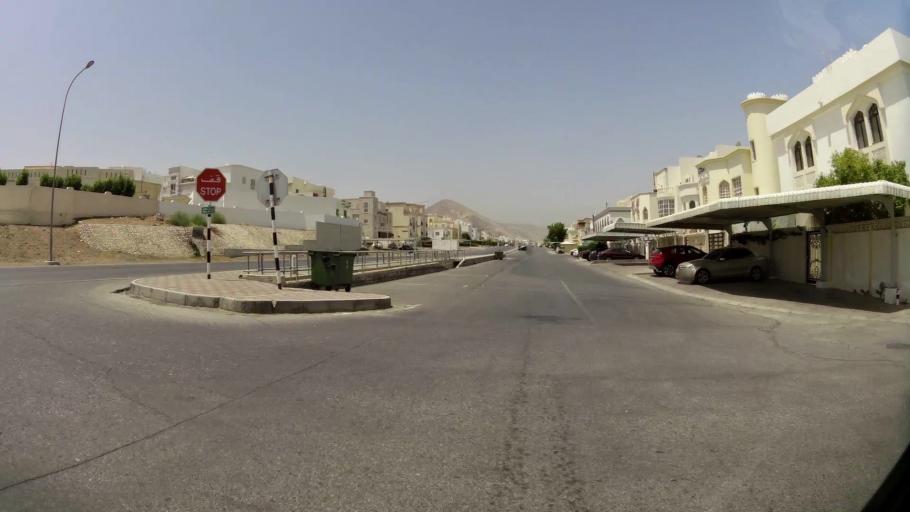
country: OM
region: Muhafazat Masqat
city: Bawshar
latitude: 23.5875
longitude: 58.4404
